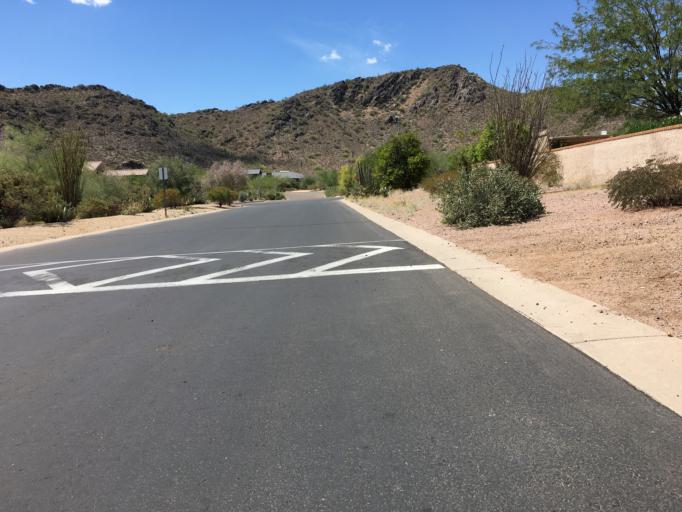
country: US
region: Arizona
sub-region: Maricopa County
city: Paradise Valley
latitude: 33.5744
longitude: -111.9897
